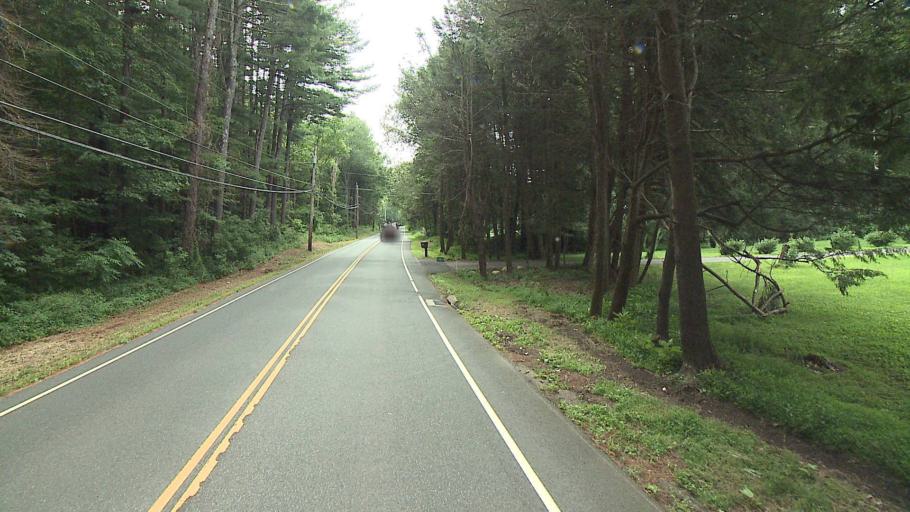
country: US
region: Connecticut
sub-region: Litchfield County
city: Woodbury
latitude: 41.5737
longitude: -73.2346
